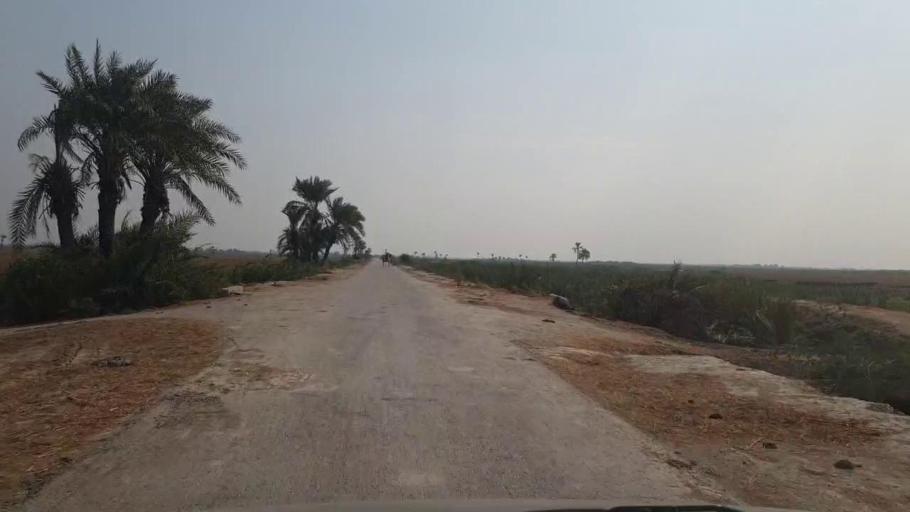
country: PK
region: Sindh
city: Tando Muhammad Khan
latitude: 25.1020
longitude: 68.3732
